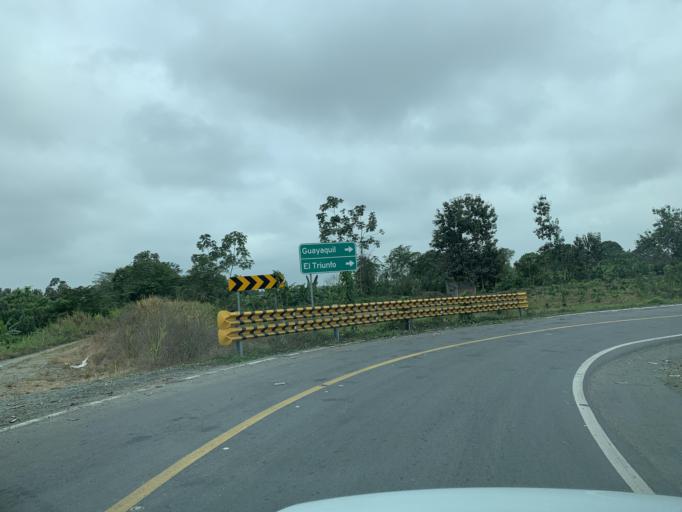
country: EC
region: Guayas
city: Coronel Marcelino Mariduena
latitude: -2.2964
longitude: -79.5044
